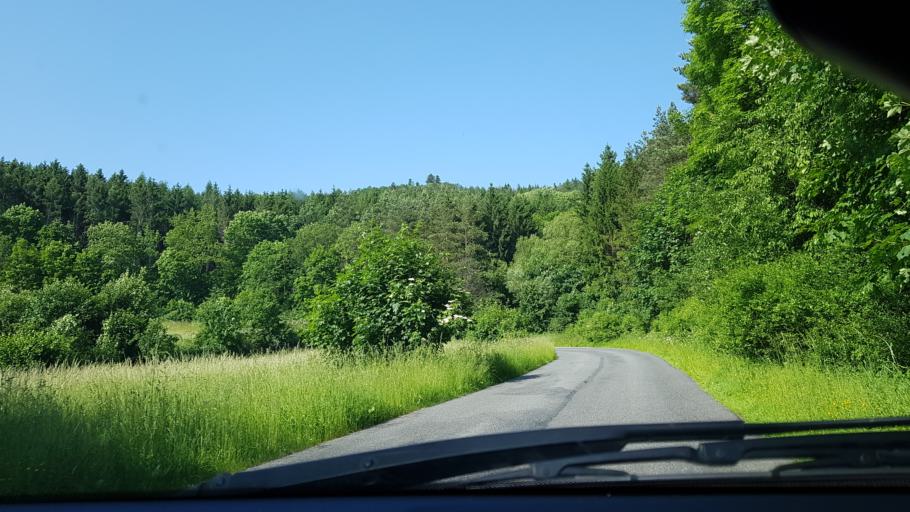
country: PL
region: Lower Silesian Voivodeship
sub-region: Powiat zabkowicki
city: Budzow
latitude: 50.5329
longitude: 16.6631
